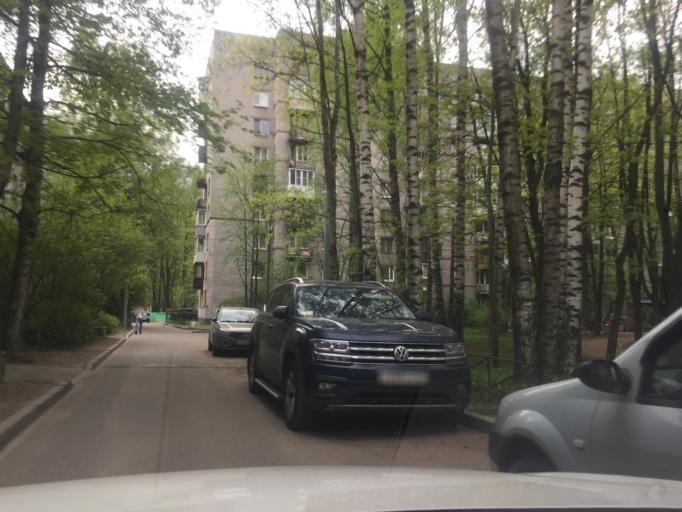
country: RU
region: Leningrad
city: Akademicheskoe
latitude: 60.0051
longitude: 30.3953
